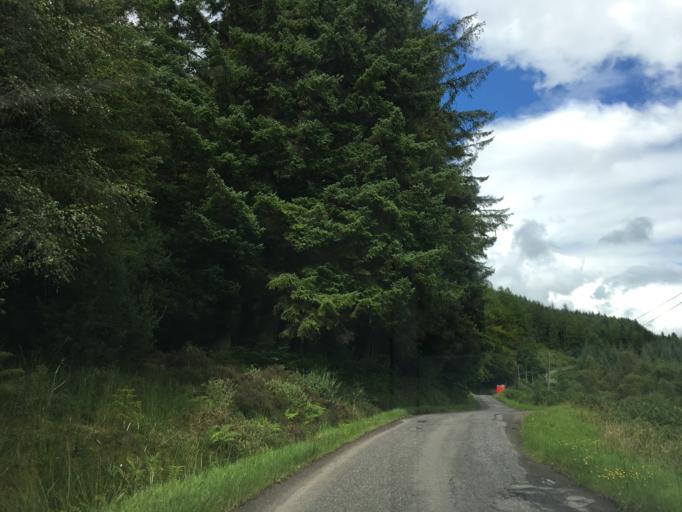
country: GB
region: Scotland
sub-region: Argyll and Bute
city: Oban
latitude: 56.2830
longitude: -5.2713
